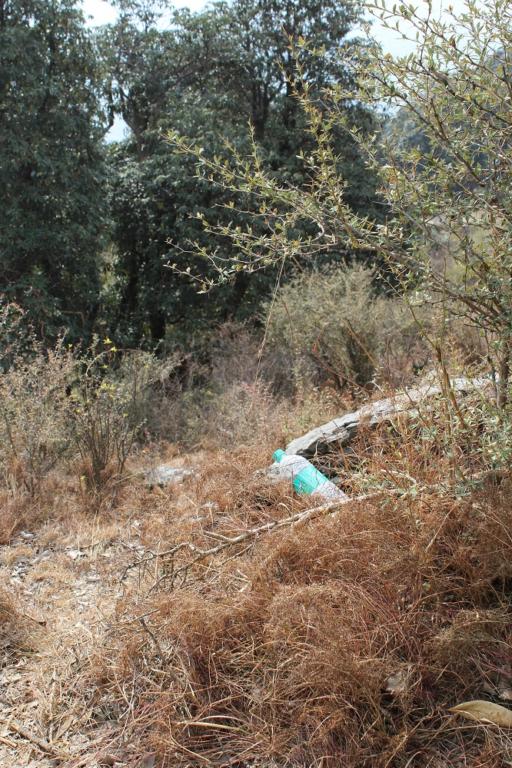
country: IN
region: Himachal Pradesh
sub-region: Mandi
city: Jogindarnagar
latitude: 32.0517
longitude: 76.7381
